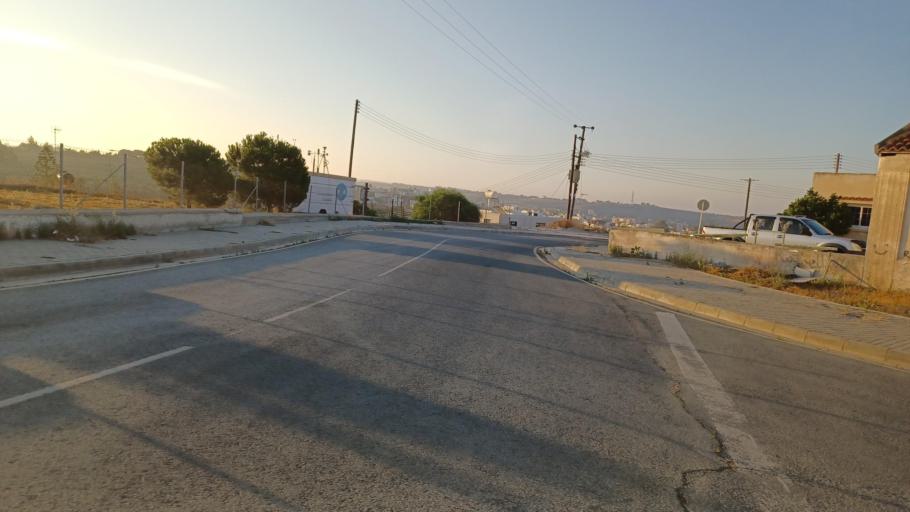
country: CY
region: Larnaka
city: Xylotymbou
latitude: 34.9962
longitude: 33.7748
